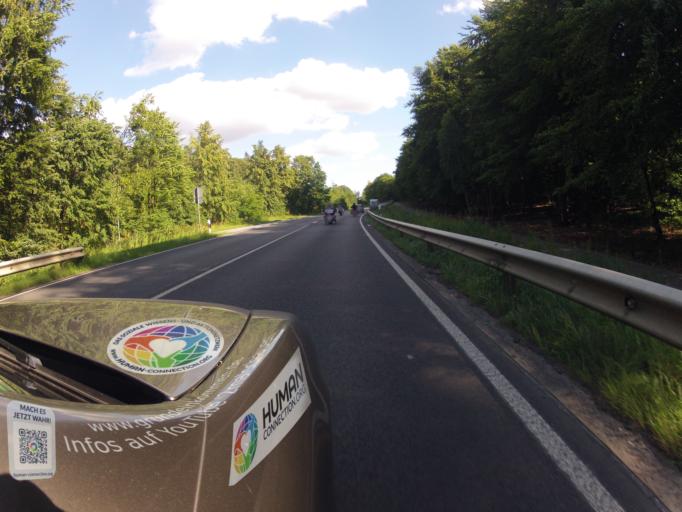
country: DE
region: Mecklenburg-Vorpommern
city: Seebad Bansin
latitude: 53.9714
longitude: 14.1175
